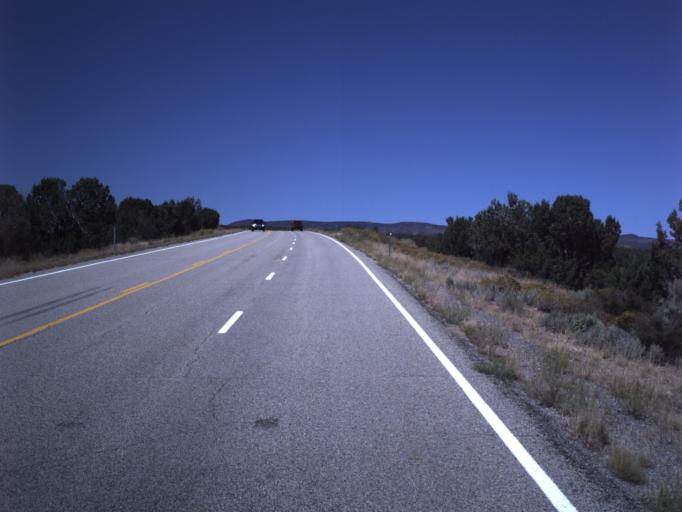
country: US
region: Utah
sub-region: San Juan County
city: Blanding
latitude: 37.5254
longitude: -109.6769
